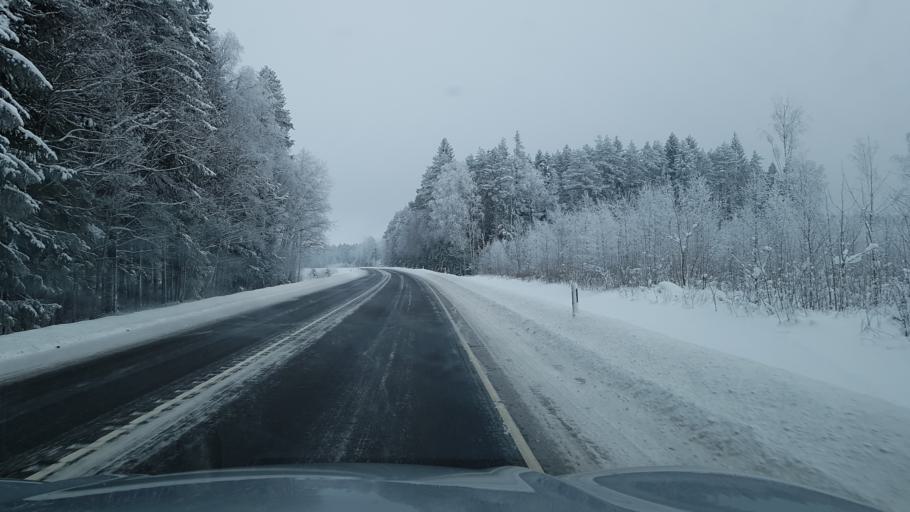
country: EE
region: Ida-Virumaa
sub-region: Johvi vald
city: Johvi
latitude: 59.2878
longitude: 27.3986
